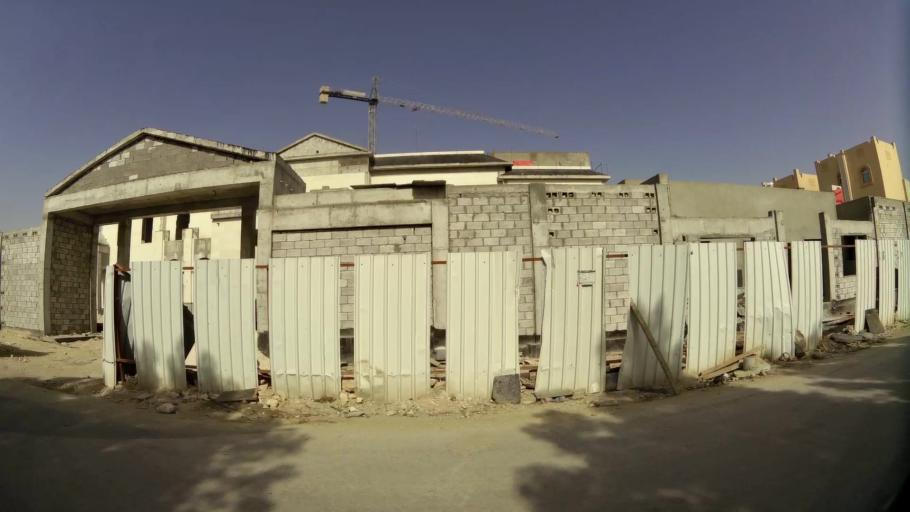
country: QA
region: Baladiyat ar Rayyan
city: Ar Rayyan
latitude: 25.3459
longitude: 51.4283
